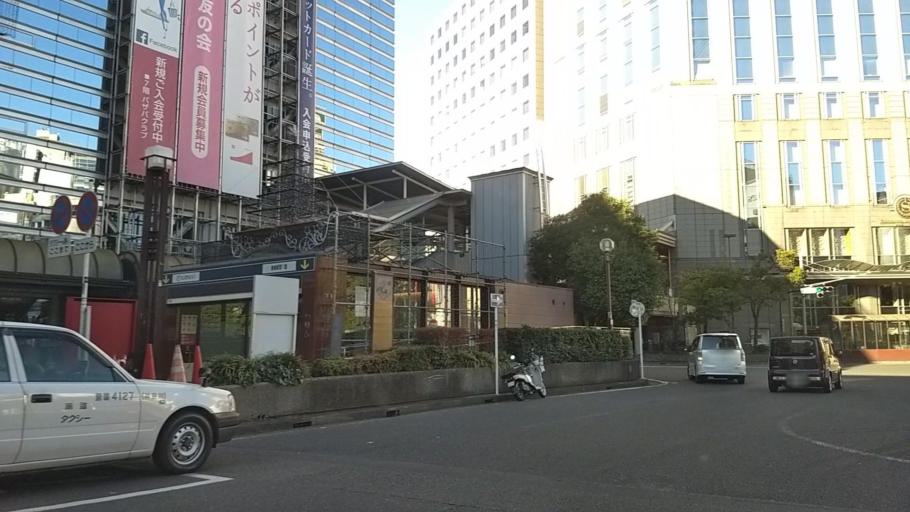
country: JP
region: Kanagawa
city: Yokohama
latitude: 35.4663
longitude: 139.6212
